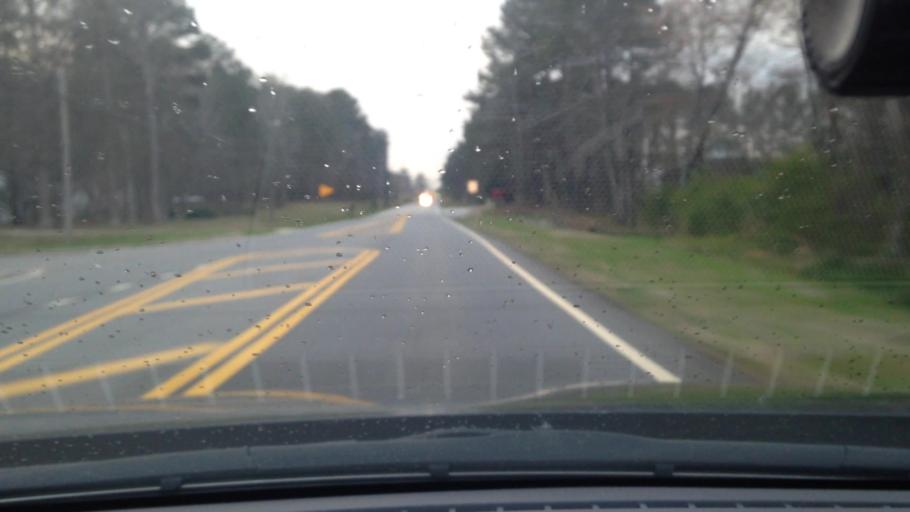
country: US
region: Georgia
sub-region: Coweta County
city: East Newnan
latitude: 33.3732
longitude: -84.7038
